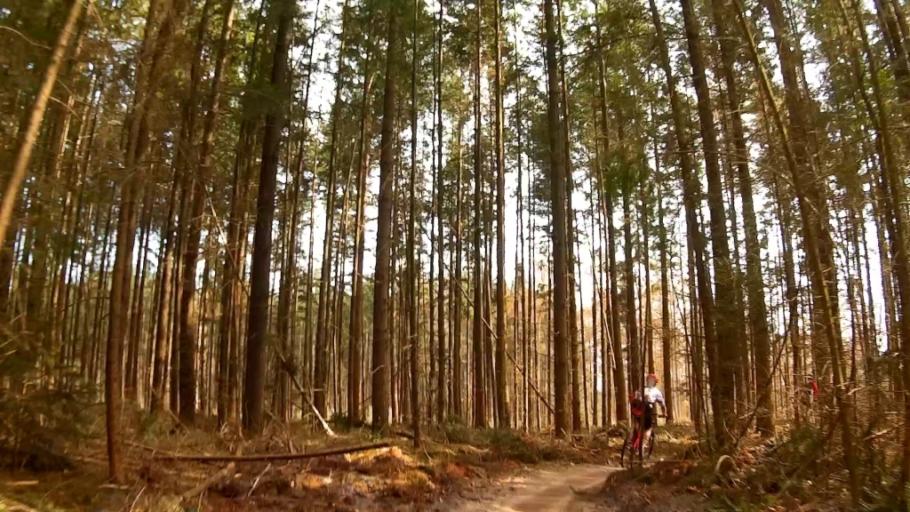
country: NL
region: Utrecht
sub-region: Gemeente Baarn
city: Baarn
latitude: 52.1956
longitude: 5.2337
